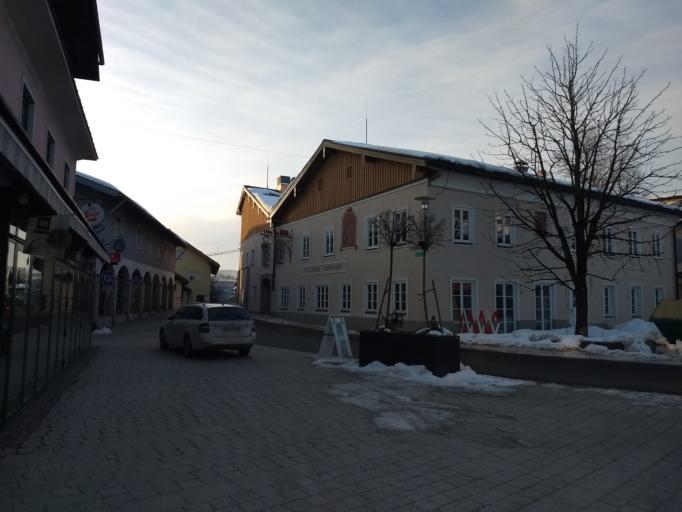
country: AT
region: Salzburg
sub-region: Politischer Bezirk Salzburg-Umgebung
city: Seekirchen am Wallersee
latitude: 47.8941
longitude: 13.1258
